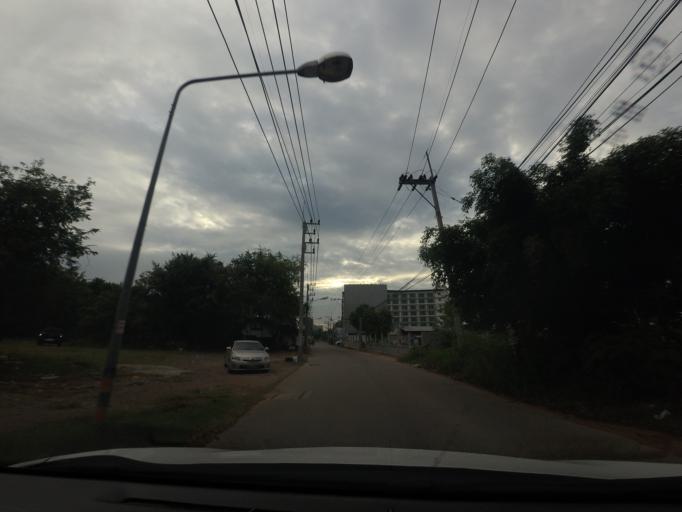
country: TH
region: Chon Buri
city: Phatthaya
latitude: 12.9022
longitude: 100.8948
